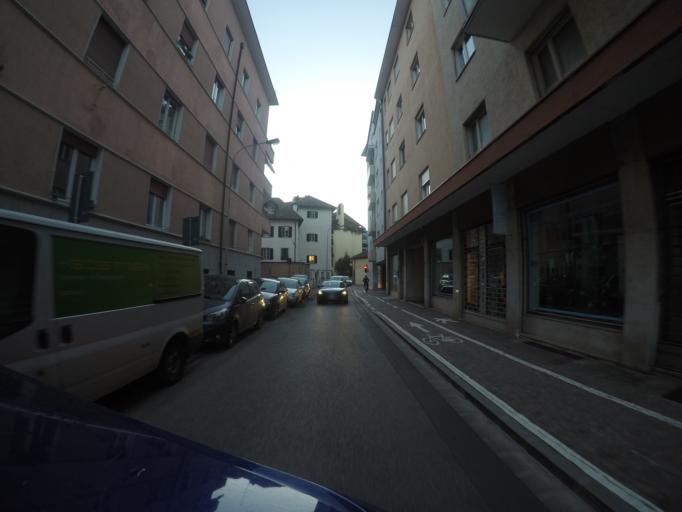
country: IT
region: Trentino-Alto Adige
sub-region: Bolzano
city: Bolzano
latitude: 46.5020
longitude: 11.3573
